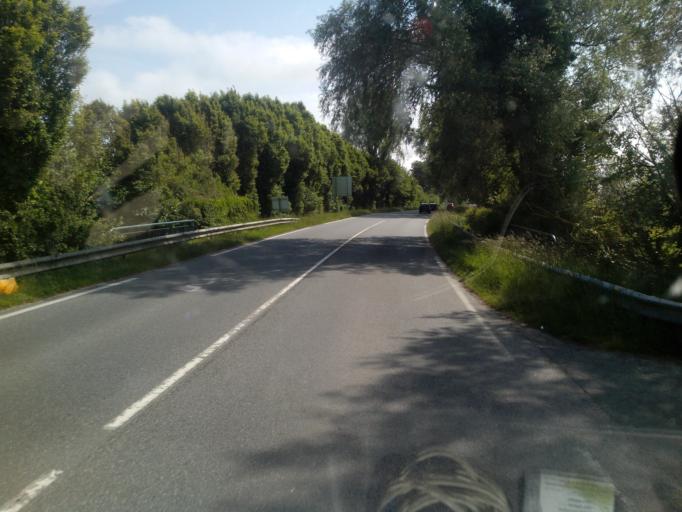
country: FR
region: Picardie
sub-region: Departement de la Somme
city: Rue
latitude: 50.2747
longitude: 1.6594
